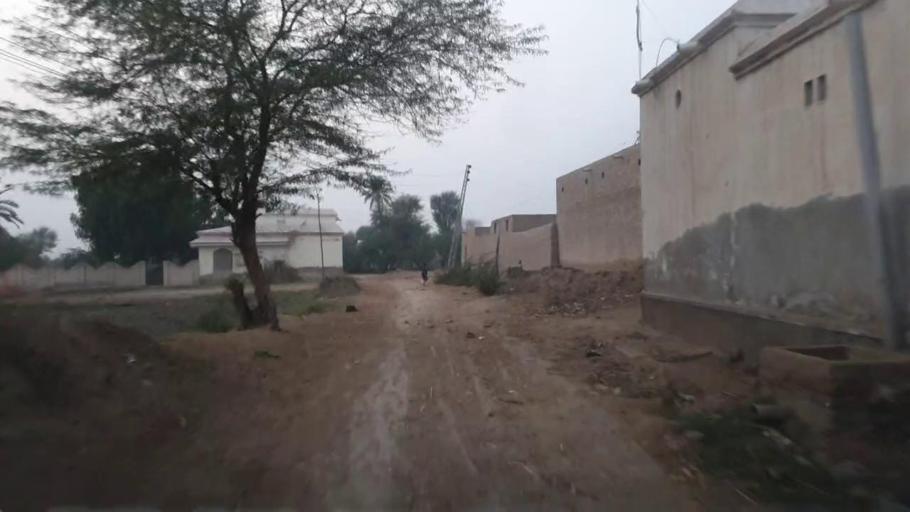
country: PK
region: Sindh
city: Karaundi
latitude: 26.9300
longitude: 68.4344
